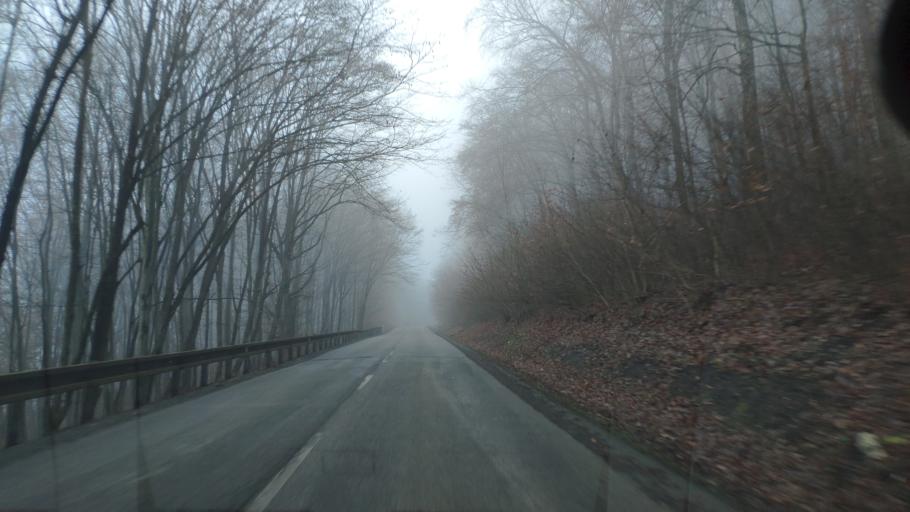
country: SK
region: Banskobystricky
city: Revuca
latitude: 48.6279
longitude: 20.2675
